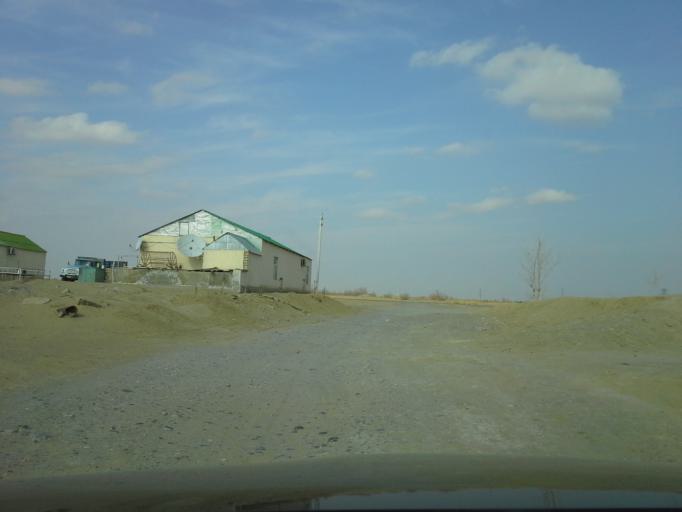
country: TM
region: Ahal
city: Ashgabat
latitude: 38.0841
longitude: 58.3797
